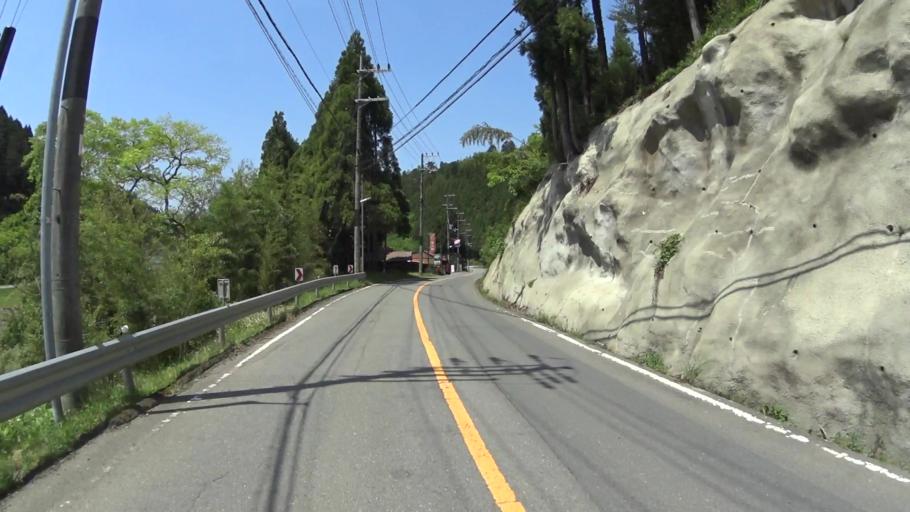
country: JP
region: Kyoto
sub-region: Kyoto-shi
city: Kamigyo-ku
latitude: 35.1987
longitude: 135.6918
